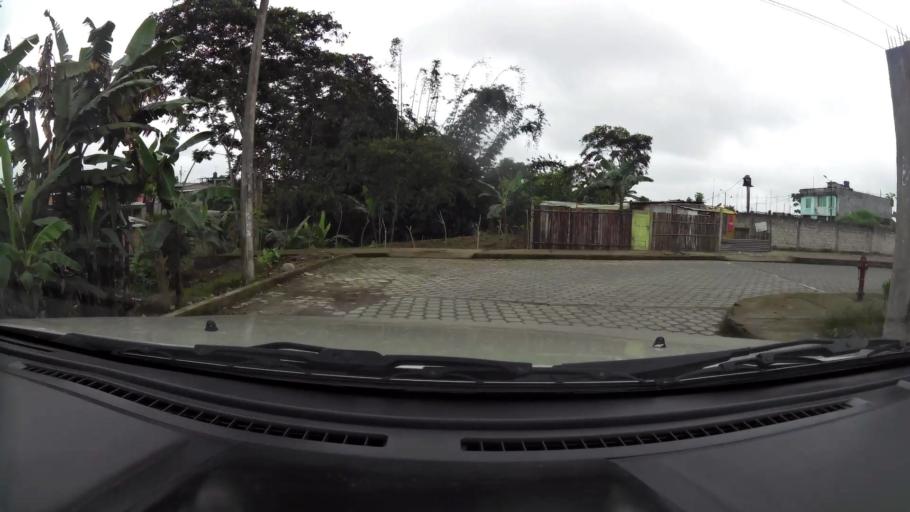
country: EC
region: Santo Domingo de los Tsachilas
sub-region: Canton Santo Domingo de los Colorados
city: Santo Domingo de los Colorados
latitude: -0.2792
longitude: -79.1907
